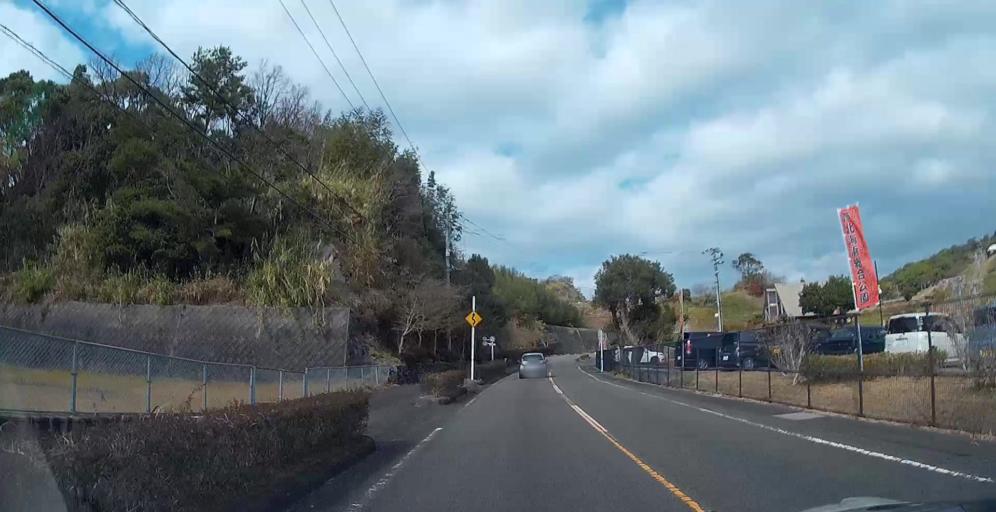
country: JP
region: Kumamoto
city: Minamata
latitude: 32.3195
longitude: 130.4707
